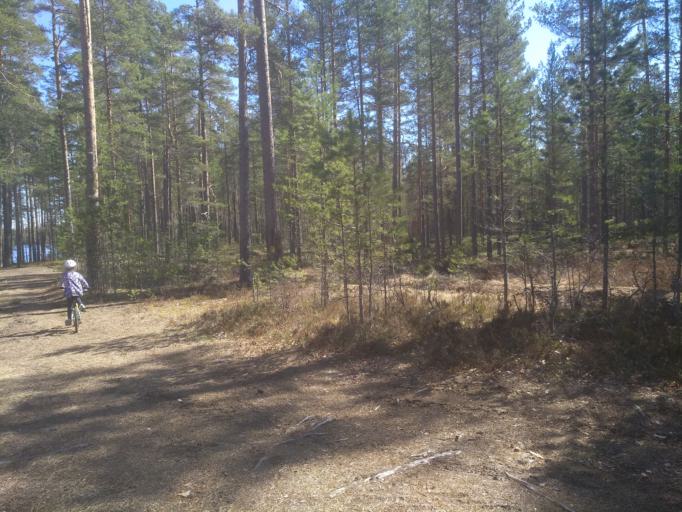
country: RU
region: Leningrad
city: Priozersk
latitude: 60.9236
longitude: 30.2591
